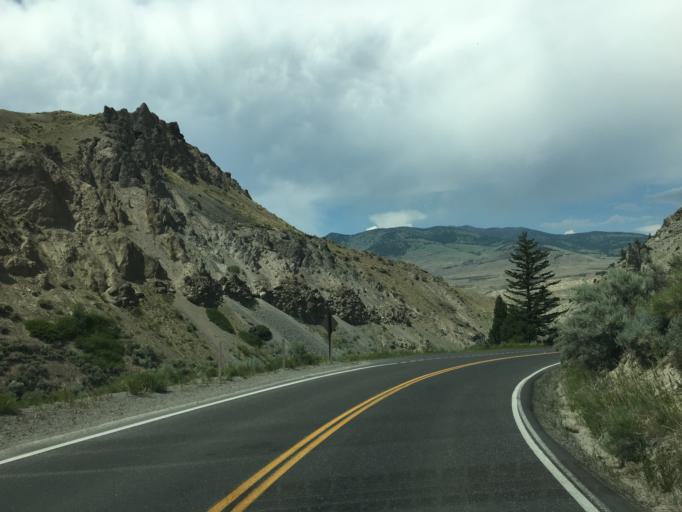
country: US
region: Montana
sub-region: Gallatin County
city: West Yellowstone
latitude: 45.0080
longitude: -110.6945
